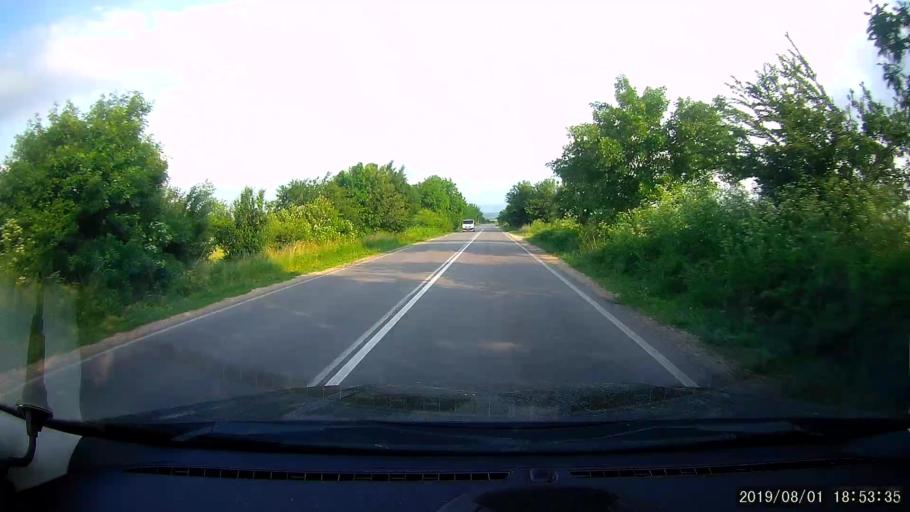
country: BG
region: Shumen
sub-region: Obshtina Shumen
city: Shumen
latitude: 43.2187
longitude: 26.9953
